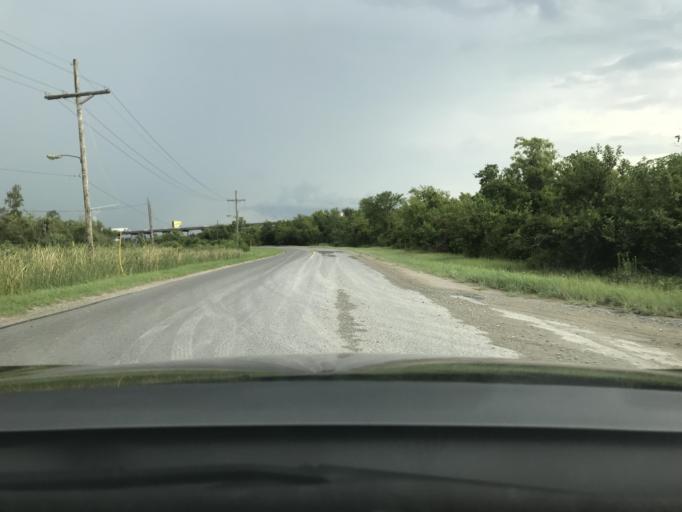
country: US
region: Louisiana
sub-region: Calcasieu Parish
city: Westlake
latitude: 30.2327
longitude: -93.2527
